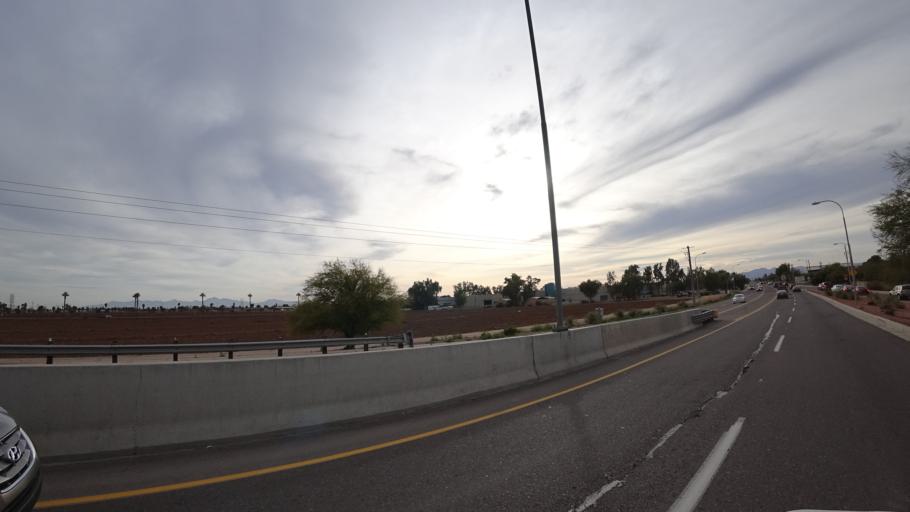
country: US
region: Arizona
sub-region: Maricopa County
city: Peoria
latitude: 33.5668
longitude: -112.2231
